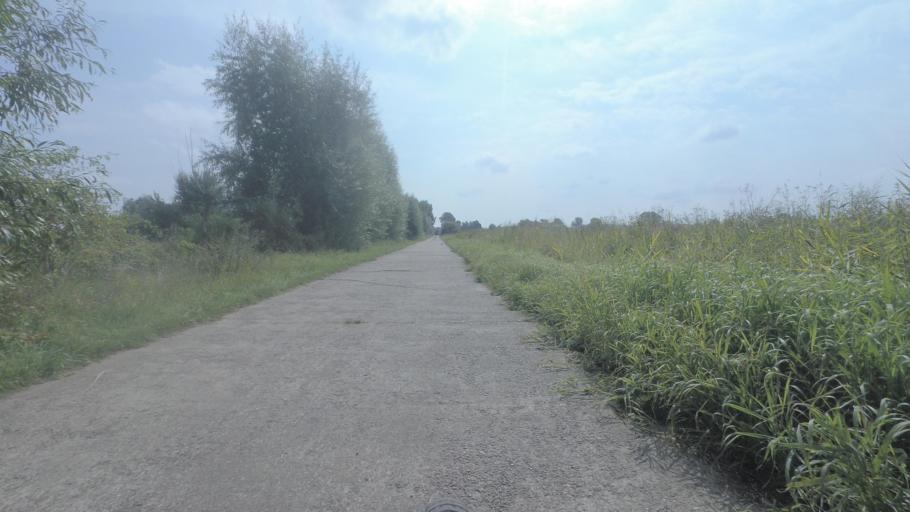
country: DE
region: Brandenburg
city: Rangsdorf
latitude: 52.2704
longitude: 13.4720
